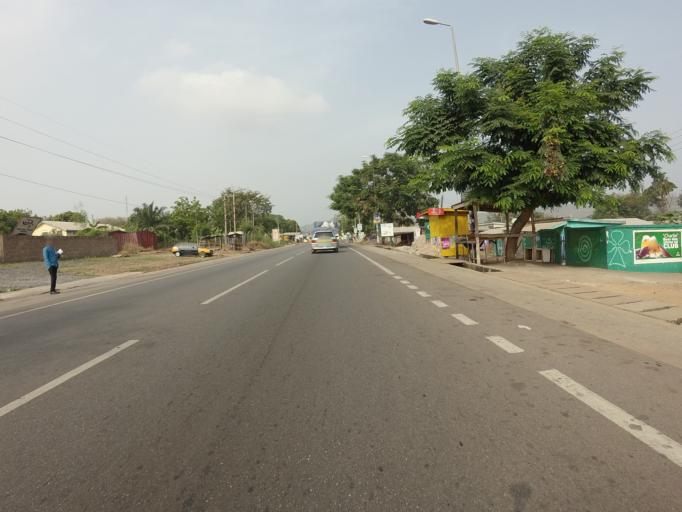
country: GH
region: Volta
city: Ho
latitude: 6.6042
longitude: 0.4789
